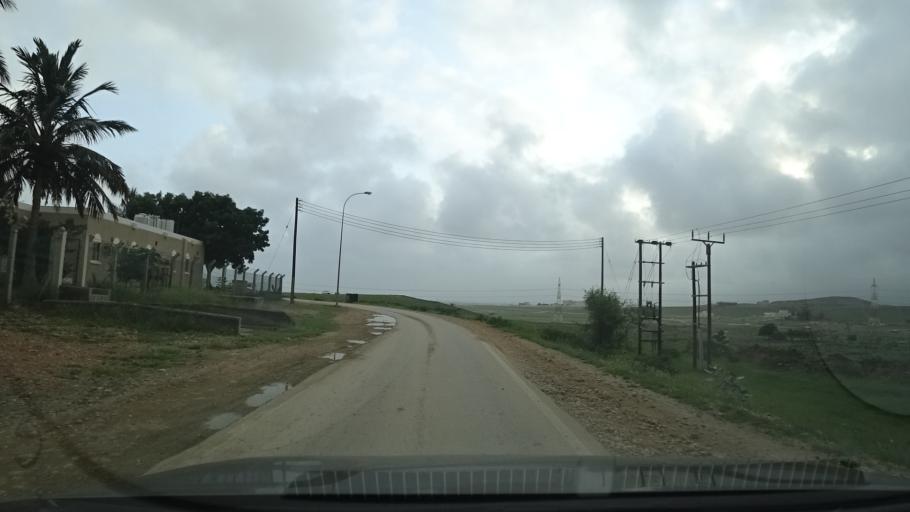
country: OM
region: Zufar
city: Salalah
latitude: 17.1199
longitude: 54.2308
